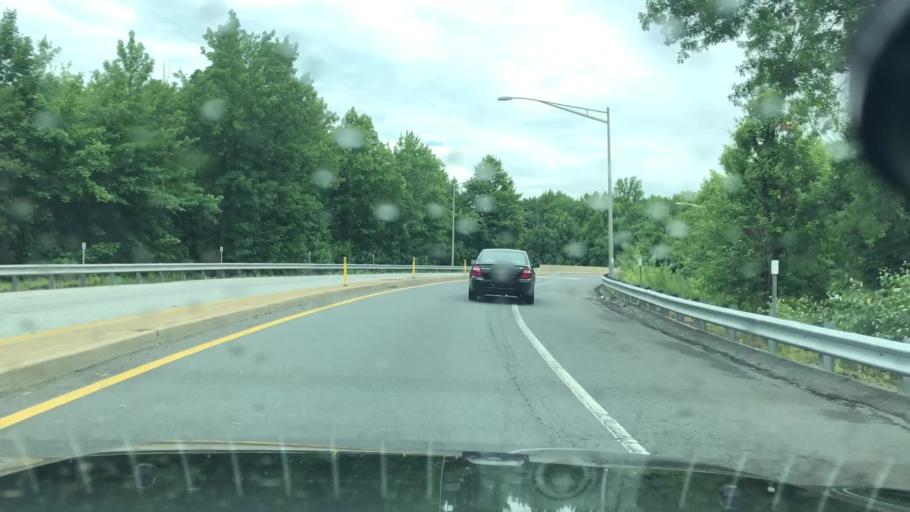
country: US
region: New Jersey
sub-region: Mercer County
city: Robbinsville
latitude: 40.1960
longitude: -74.6111
